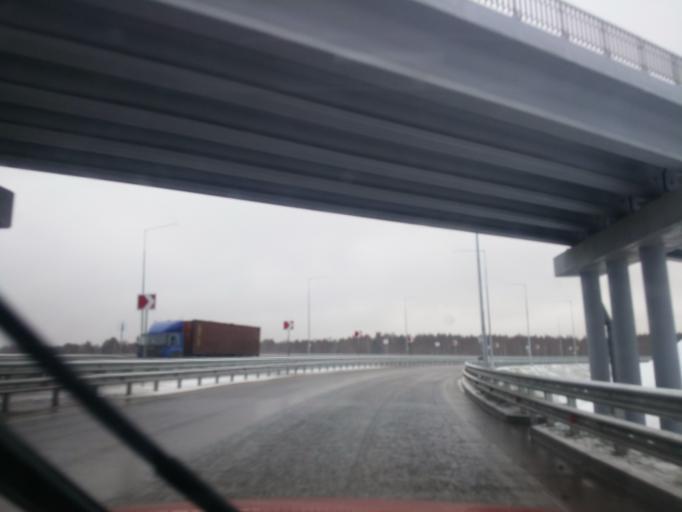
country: RU
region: Tverskaya
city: Likhoslavl'
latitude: 56.9513
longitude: 35.5143
